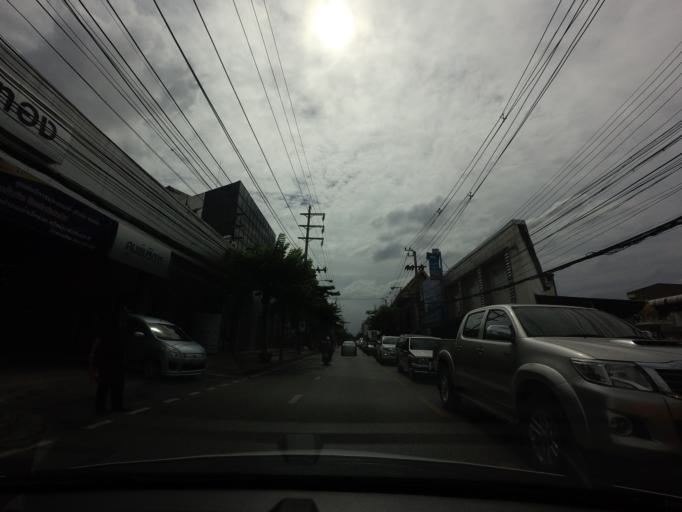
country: TH
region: Bangkok
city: Chom Thong
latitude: 13.6942
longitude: 100.4802
